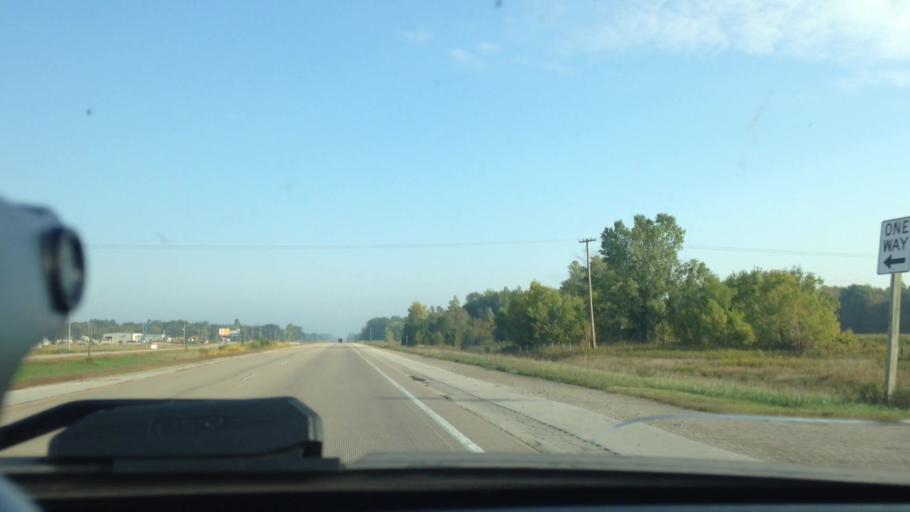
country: US
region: Wisconsin
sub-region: Oconto County
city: Oconto Falls
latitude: 44.9936
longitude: -88.0451
